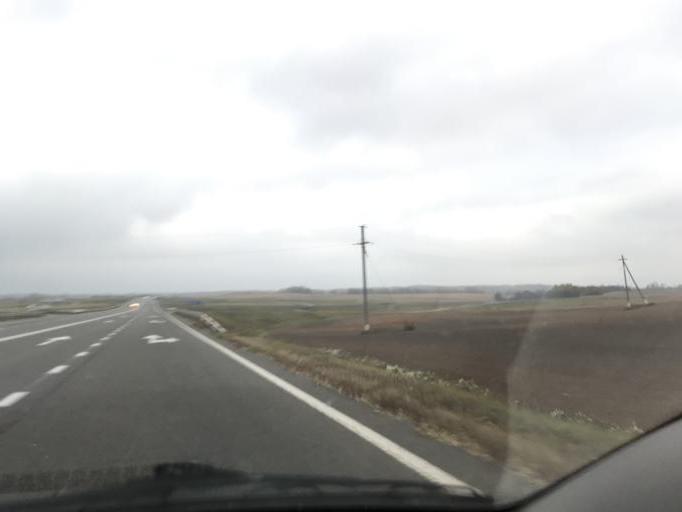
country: BY
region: Vitebsk
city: Vitebsk
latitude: 55.1514
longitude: 30.0663
